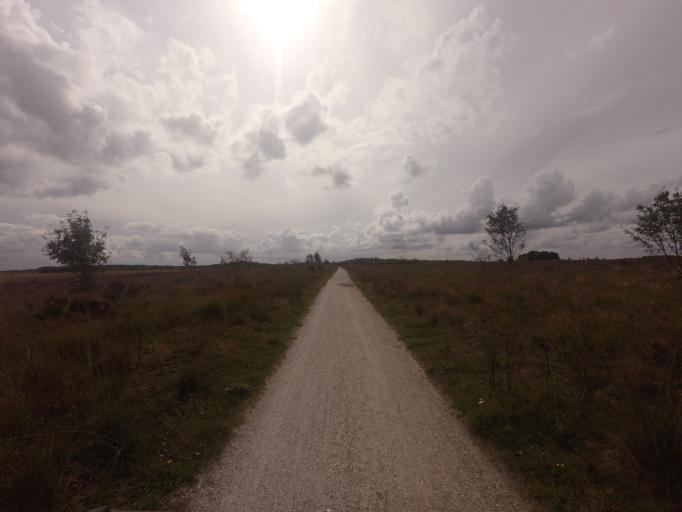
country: NL
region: Groningen
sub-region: Gemeente Leek
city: Leek
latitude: 52.9995
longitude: 6.3828
